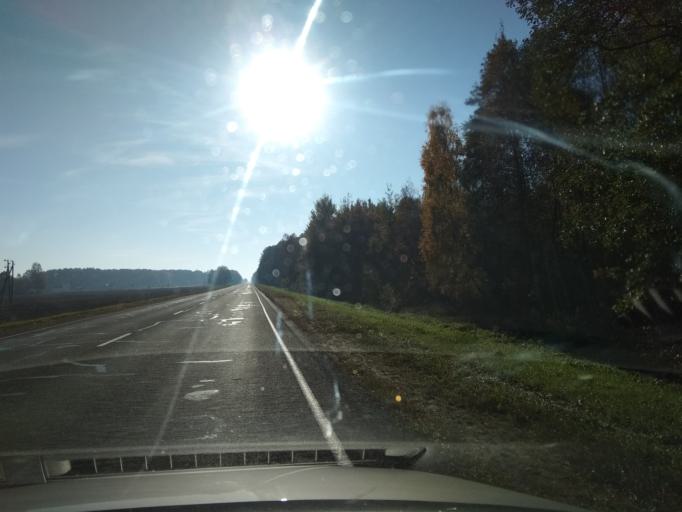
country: BY
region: Brest
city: Malaryta
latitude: 51.8809
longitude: 24.1622
